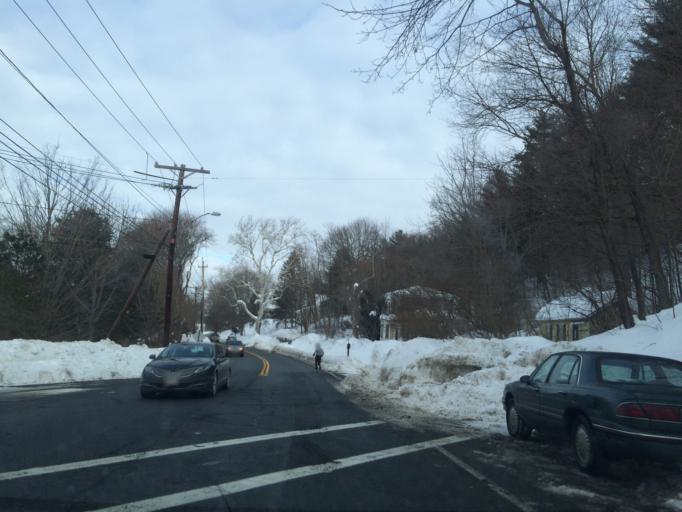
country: US
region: Massachusetts
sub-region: Middlesex County
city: Weston
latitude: 42.3874
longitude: -71.2880
